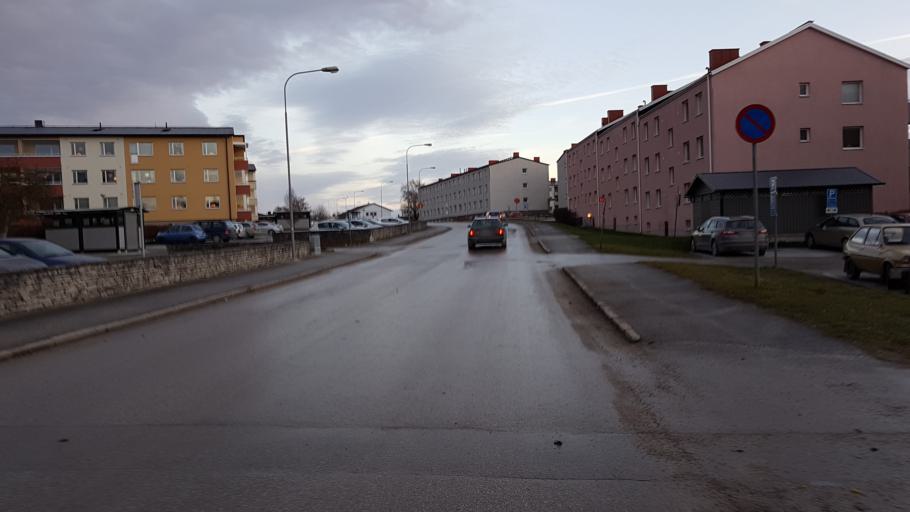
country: SE
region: Gotland
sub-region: Gotland
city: Visby
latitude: 57.6219
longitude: 18.2809
